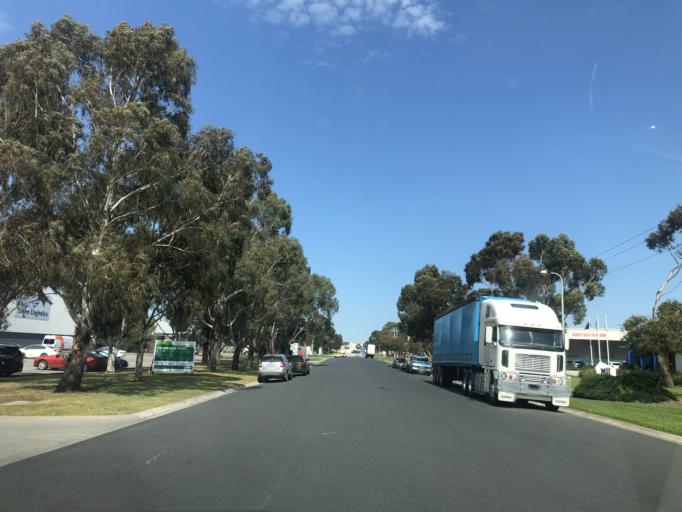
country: AU
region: Victoria
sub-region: Casey
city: Hampton Park
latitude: -38.0380
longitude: 145.2420
